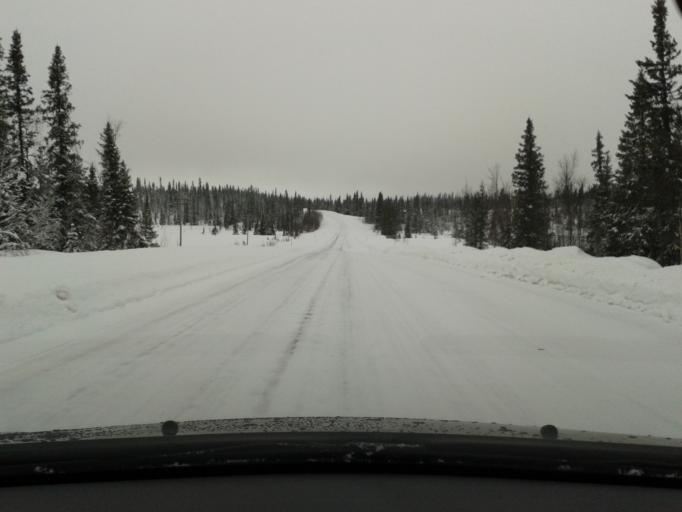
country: SE
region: Vaesterbotten
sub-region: Vilhelmina Kommun
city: Sjoberg
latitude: 65.1563
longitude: 15.8638
